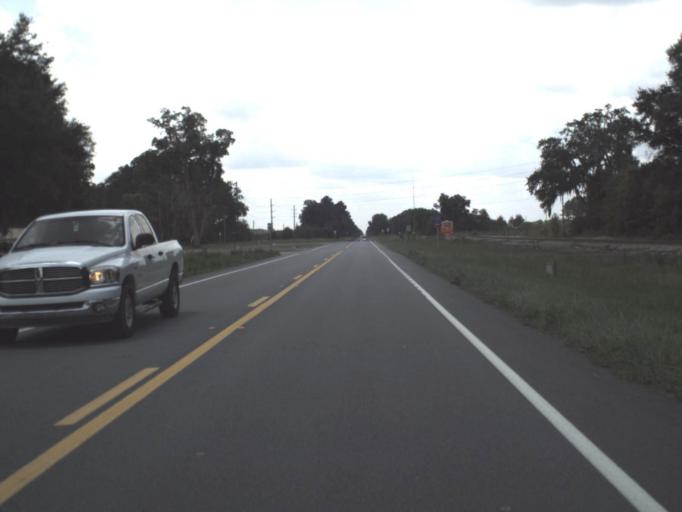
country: US
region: Florida
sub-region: Hamilton County
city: Jasper
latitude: 30.3989
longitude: -82.8338
